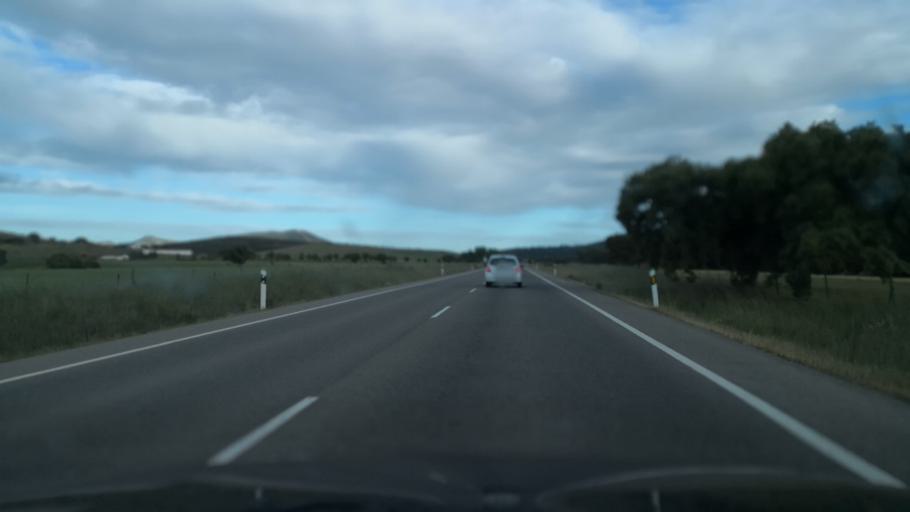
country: ES
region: Extremadura
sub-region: Provincia de Caceres
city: Pedroso de Acim
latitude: 39.8541
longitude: -6.4212
